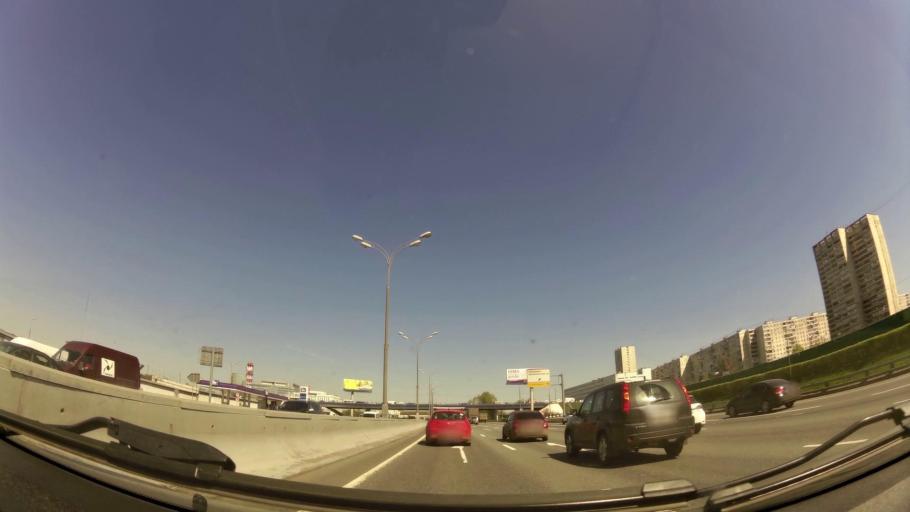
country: RU
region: Moscow
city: Strogino
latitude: 55.8073
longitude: 37.3879
